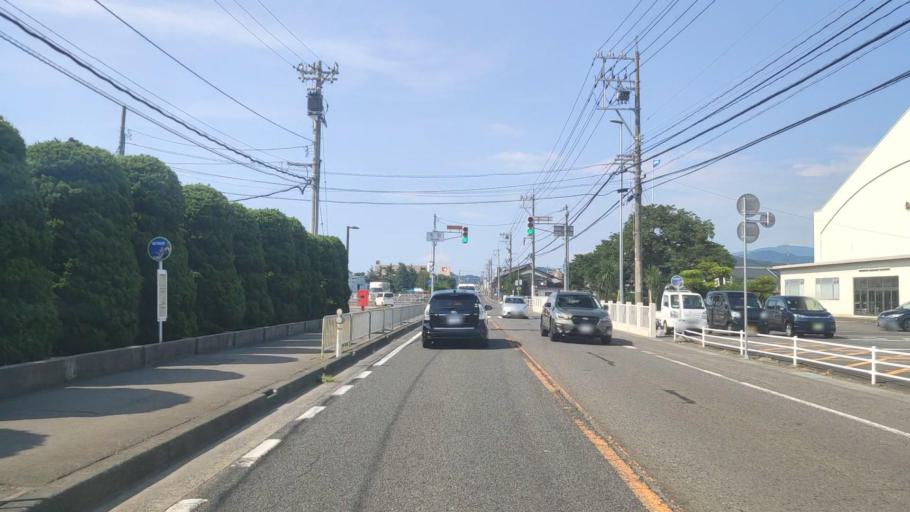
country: JP
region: Fukui
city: Tsuruga
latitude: 35.6393
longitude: 136.0708
